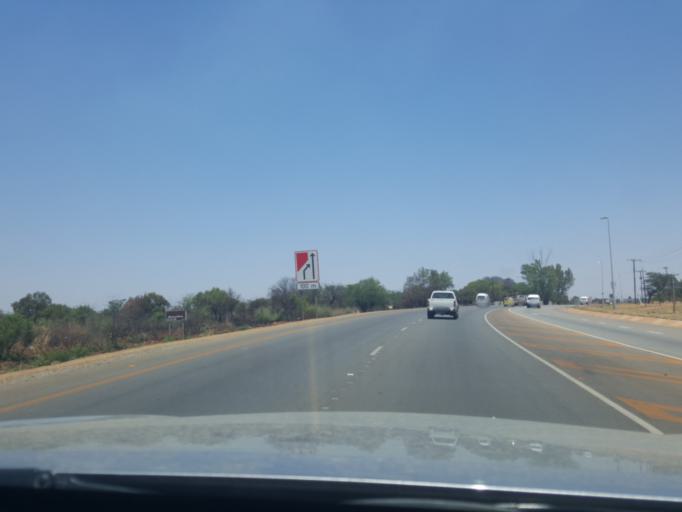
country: ZA
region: North-West
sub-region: Ngaka Modiri Molema District Municipality
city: Zeerust
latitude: -25.5525
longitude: 26.0714
